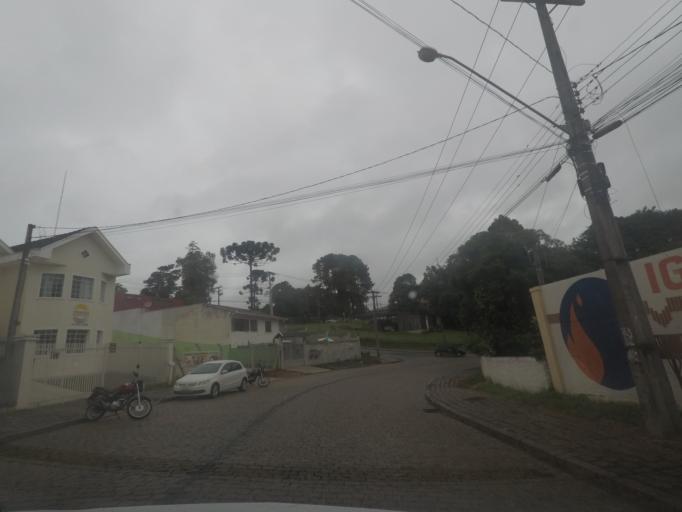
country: BR
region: Parana
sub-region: Quatro Barras
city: Quatro Barras
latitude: -25.3700
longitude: -49.0760
